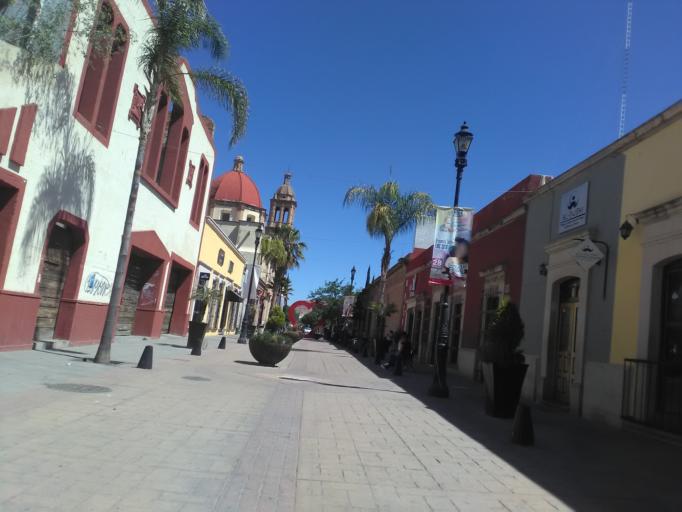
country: MX
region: Durango
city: Victoria de Durango
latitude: 24.0289
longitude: -104.6710
